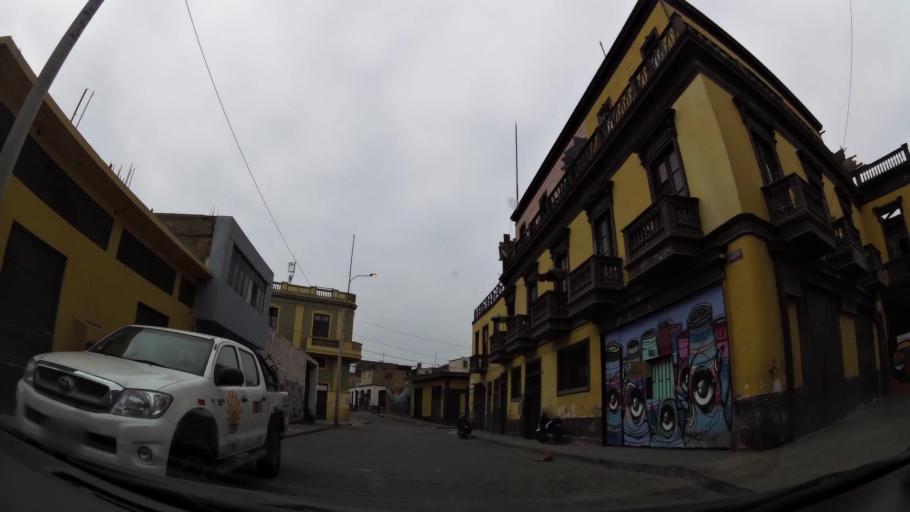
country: PE
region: Callao
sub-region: Callao
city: Callao
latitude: -12.0604
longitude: -77.1459
